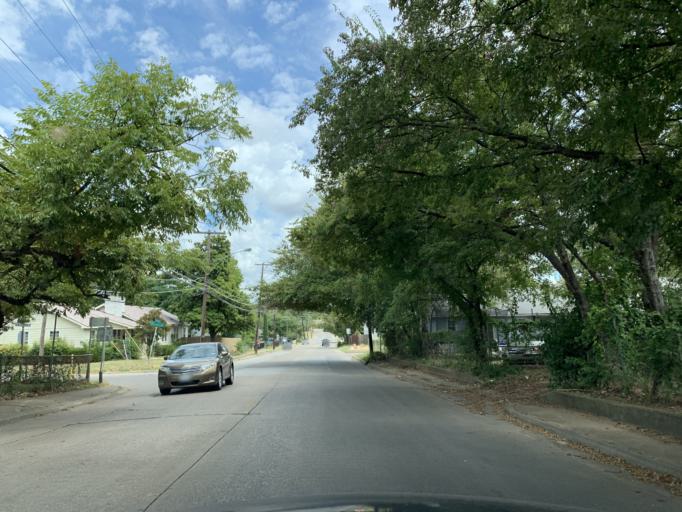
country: US
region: Texas
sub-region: Dallas County
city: Cockrell Hill
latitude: 32.7349
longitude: -96.8800
